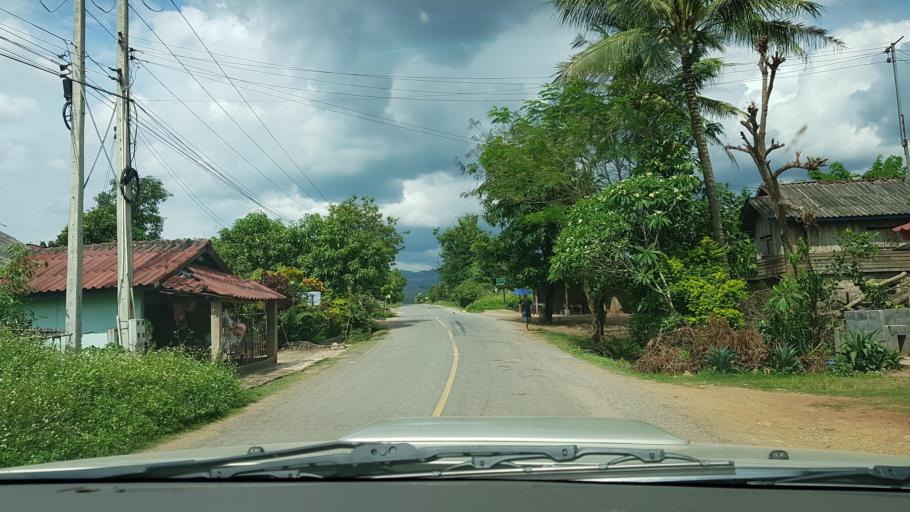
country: LA
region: Loungnamtha
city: Muang Nale
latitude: 20.2837
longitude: 101.6168
